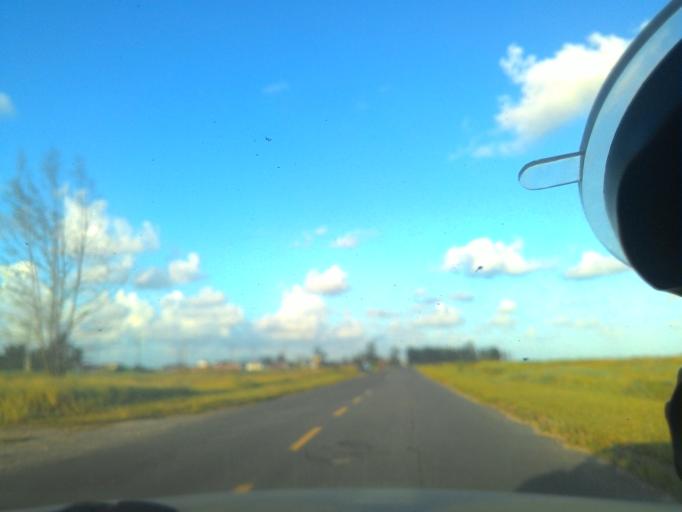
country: BR
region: Sao Paulo
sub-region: Iguape
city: Iguape
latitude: -24.8028
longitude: -47.6325
